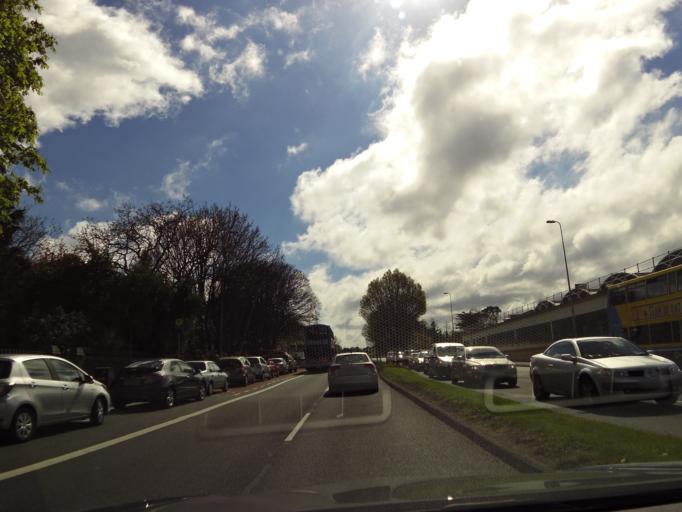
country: IE
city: Clonskeagh
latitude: 53.3189
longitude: -6.2310
